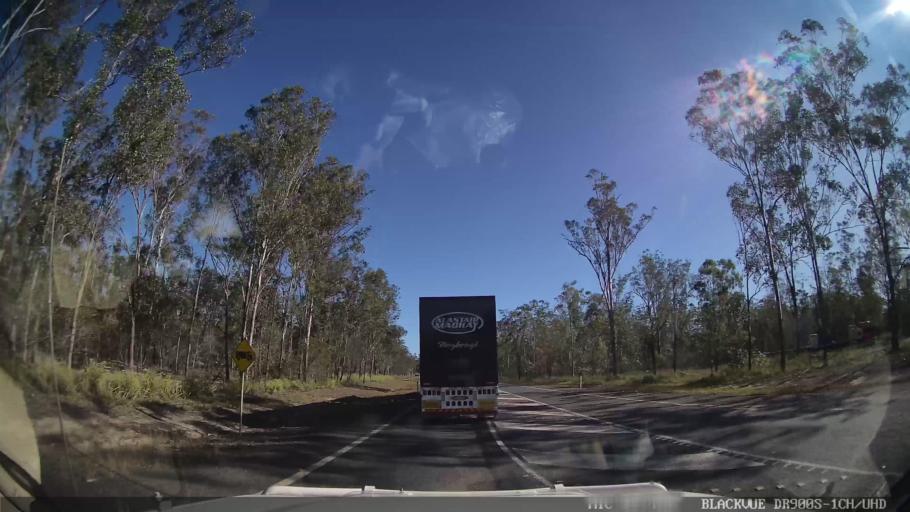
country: AU
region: Queensland
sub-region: Bundaberg
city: Childers
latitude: -25.2117
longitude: 152.0834
